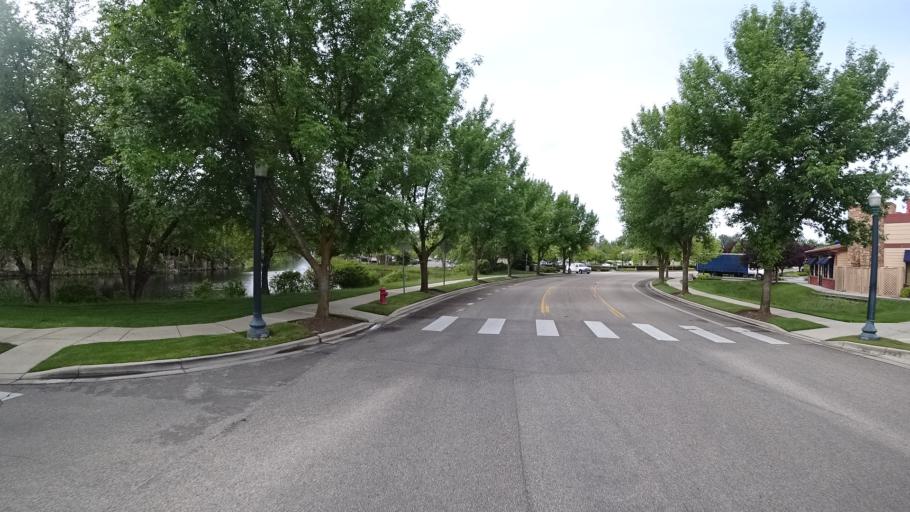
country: US
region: Idaho
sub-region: Ada County
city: Eagle
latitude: 43.6883
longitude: -116.3520
